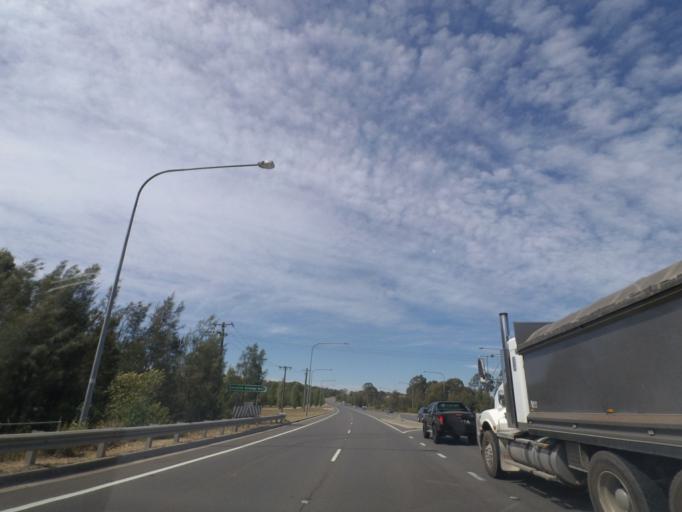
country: AU
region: New South Wales
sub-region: Camden
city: Narellan
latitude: -34.0365
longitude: 150.7460
